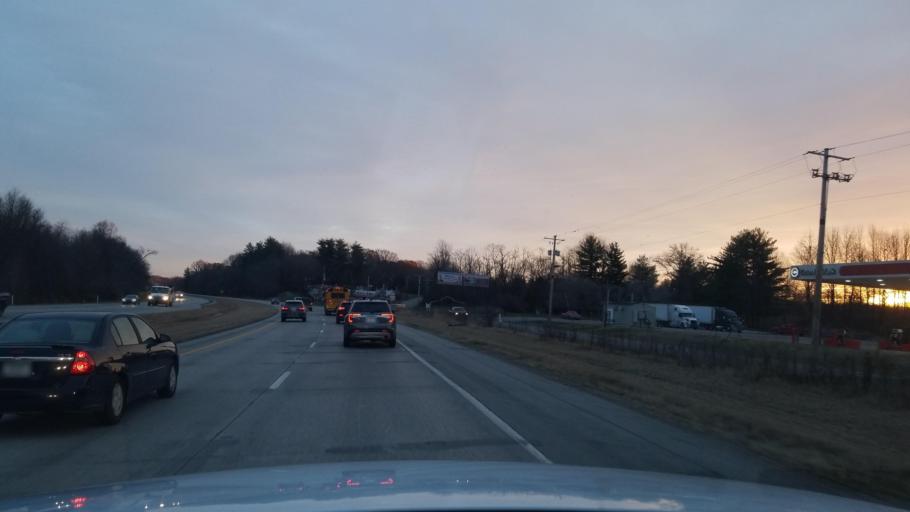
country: US
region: Indiana
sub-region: Vanderburgh County
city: Evansville
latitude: 37.9424
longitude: -87.7181
